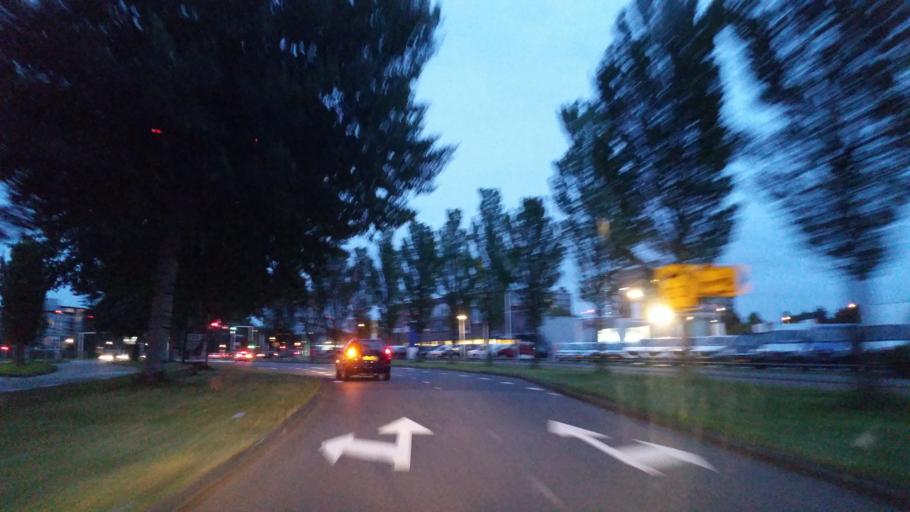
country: NL
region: Friesland
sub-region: Gemeente Leeuwarden
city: Leeuwarden
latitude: 53.2125
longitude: 5.8112
